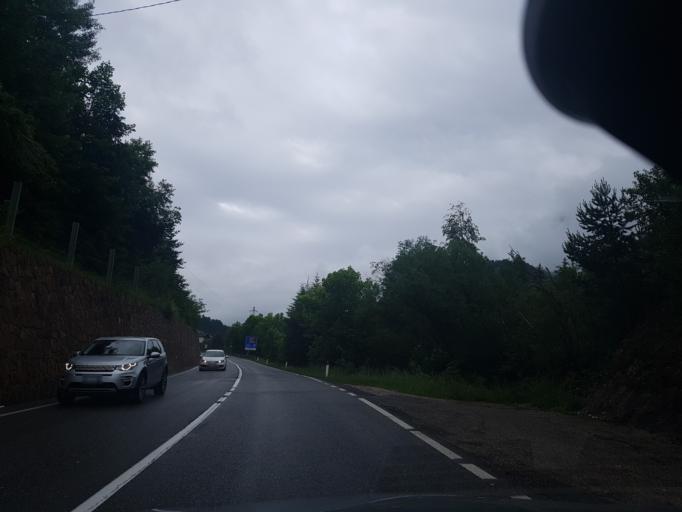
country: IT
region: Trentino-Alto Adige
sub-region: Bolzano
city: Ortisei
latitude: 46.5643
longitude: 11.6951
